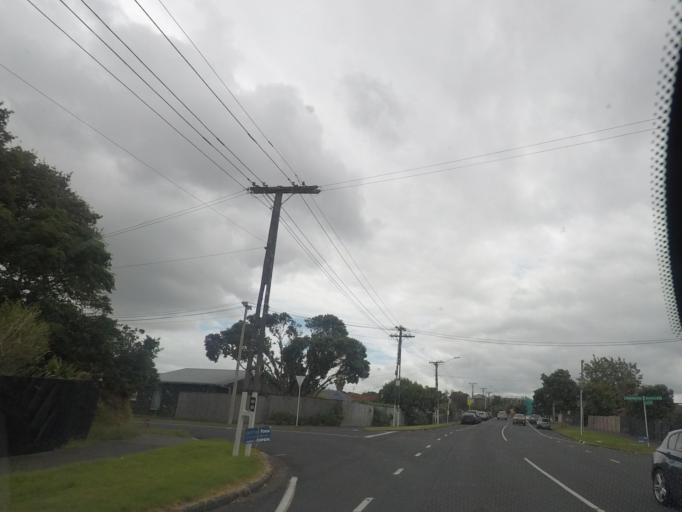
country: NZ
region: Auckland
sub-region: Auckland
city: Tamaki
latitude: -36.8701
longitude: 174.8624
